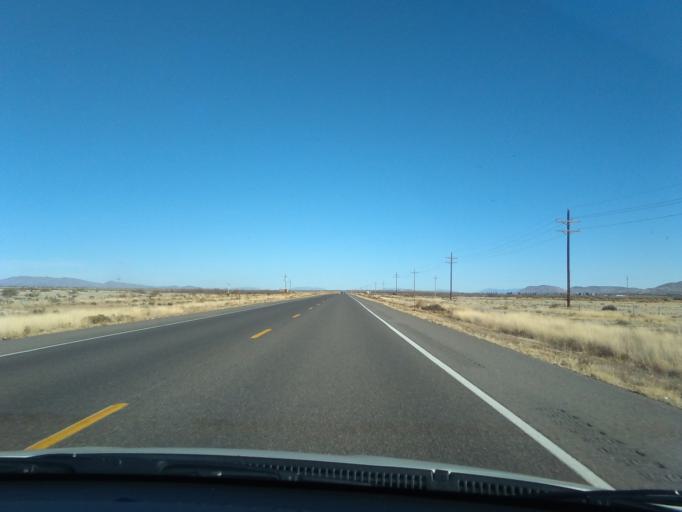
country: US
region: New Mexico
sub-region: Dona Ana County
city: Hatch
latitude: 32.5972
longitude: -107.3372
